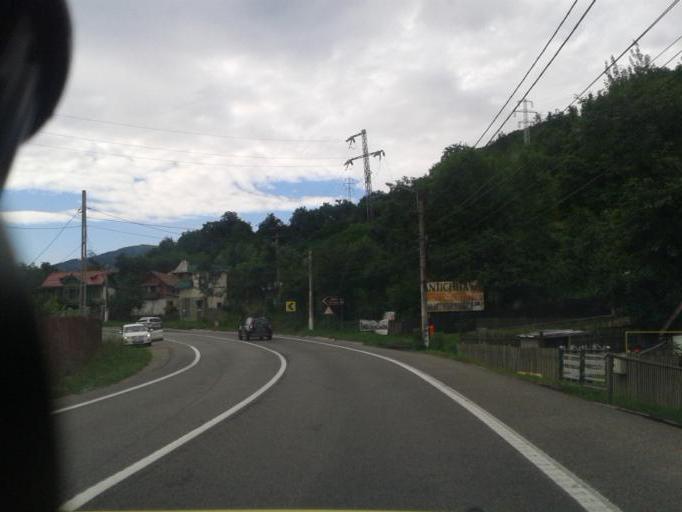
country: RO
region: Prahova
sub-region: Comuna Comarnic
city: Posada
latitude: 45.2699
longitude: 25.6242
